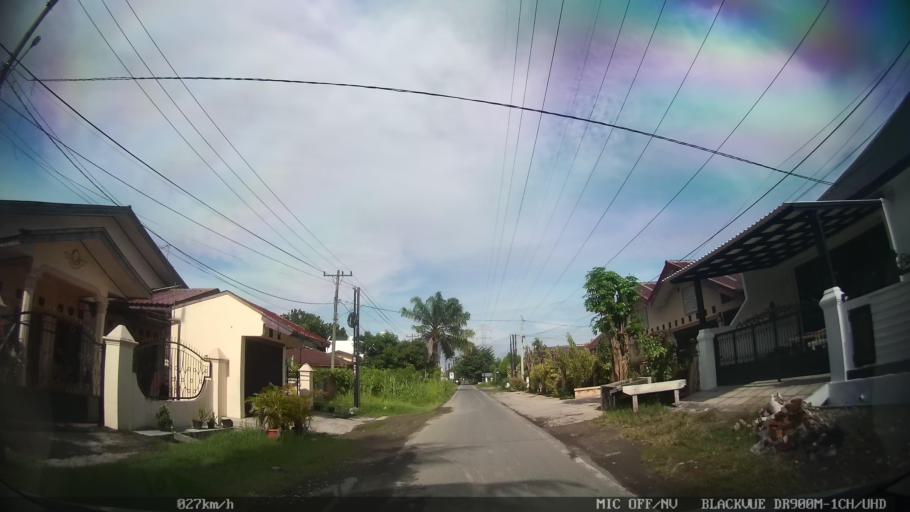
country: ID
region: North Sumatra
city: Medan
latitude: 3.6169
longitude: 98.6625
